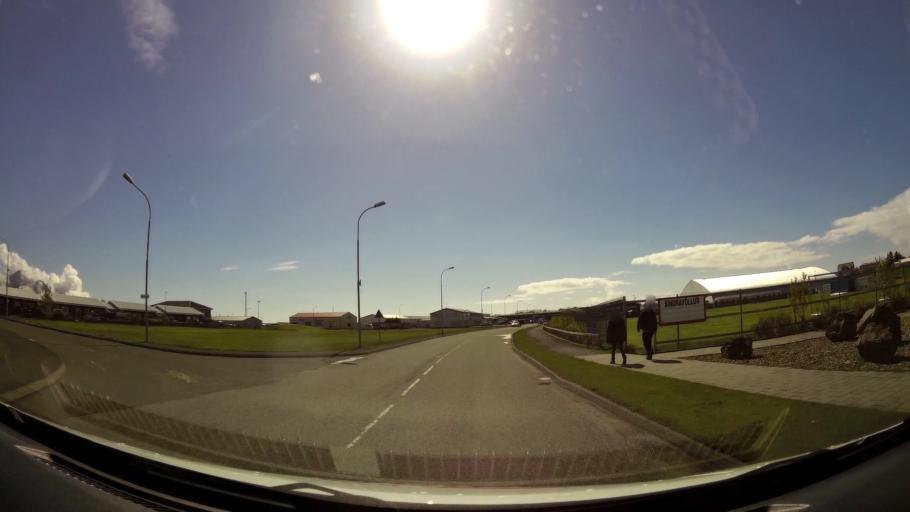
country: IS
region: East
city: Hoefn
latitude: 64.2539
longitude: -15.2059
